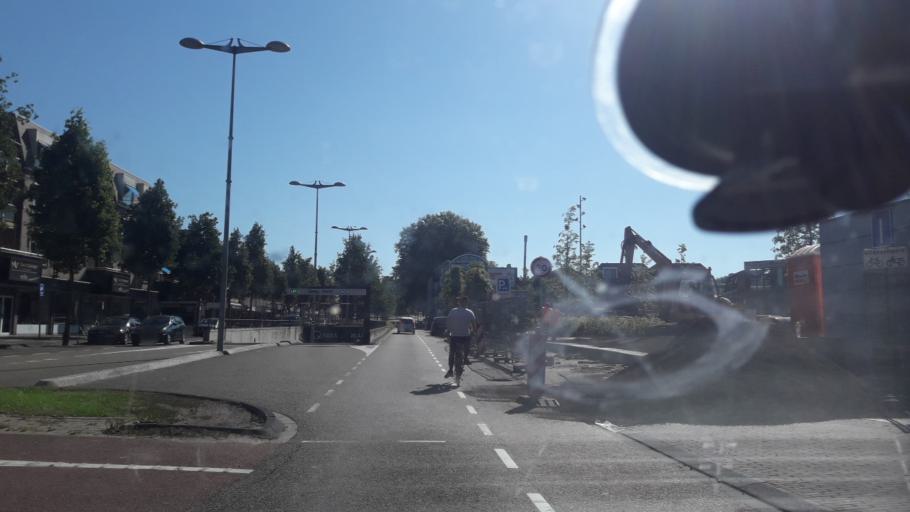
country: NL
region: Gelderland
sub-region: Gemeente Ede
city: Ede
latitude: 52.0468
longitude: 5.6688
